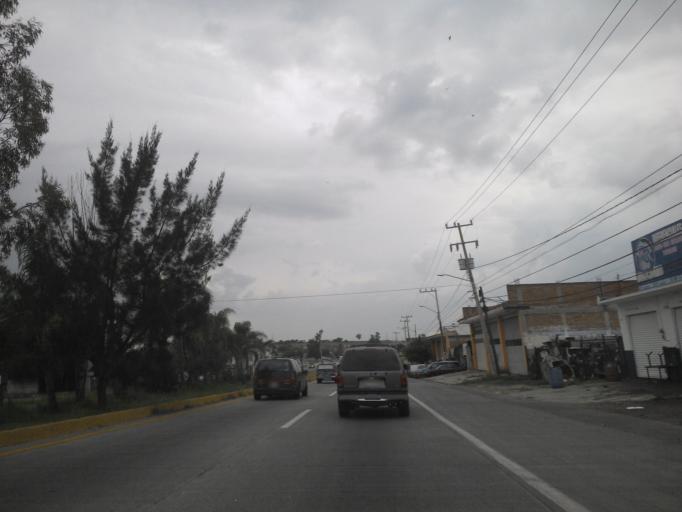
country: MX
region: Jalisco
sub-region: Zapotlanejo
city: La Mezquitera
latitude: 20.5796
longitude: -103.1257
